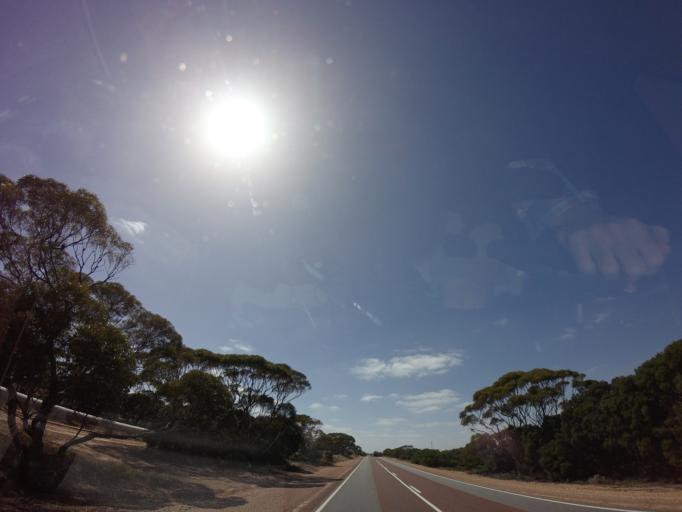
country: AU
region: South Australia
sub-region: Kimba
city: Caralue
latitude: -33.0826
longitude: 135.4983
